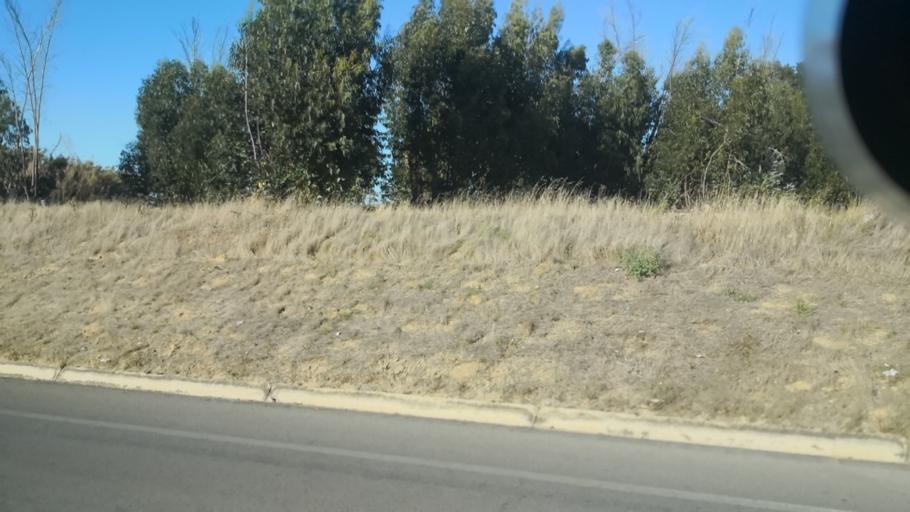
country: PT
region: Setubal
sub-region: Moita
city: Moita
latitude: 38.6340
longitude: -8.9705
